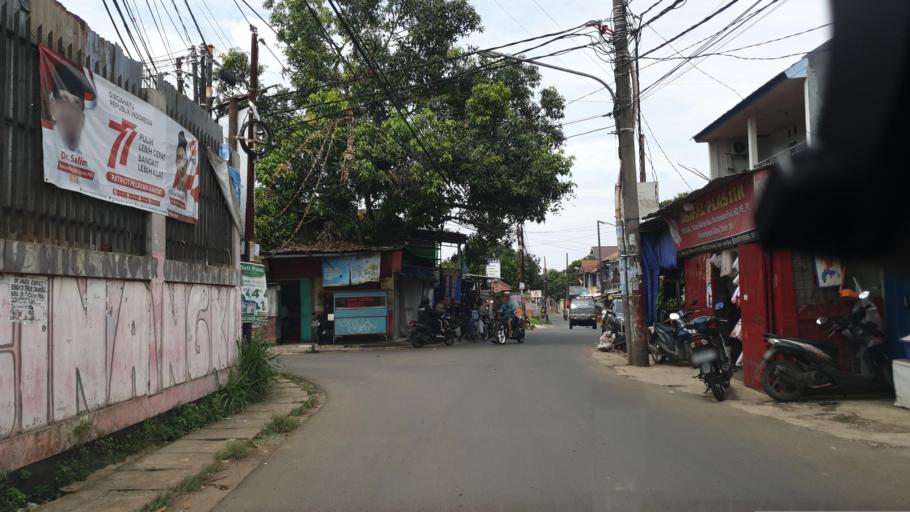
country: ID
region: West Java
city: Pamulang
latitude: -6.3686
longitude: 106.7589
